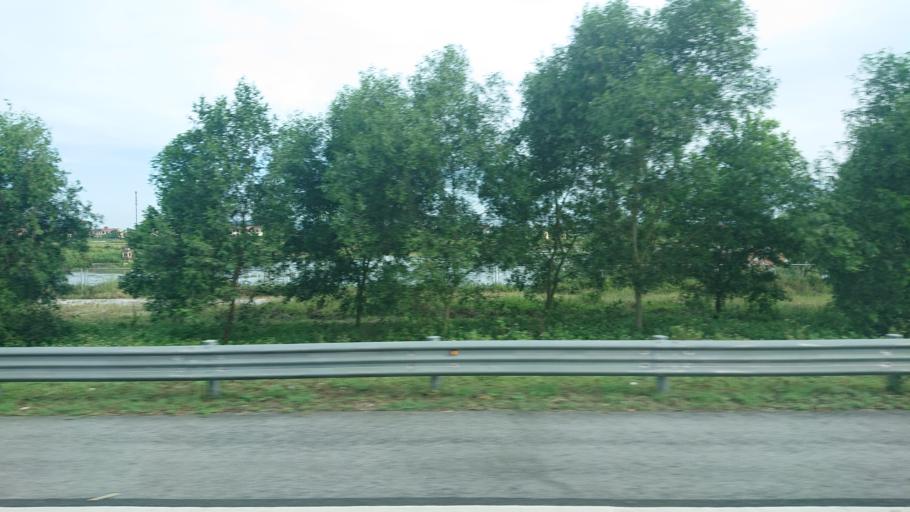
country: VN
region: Hai Phong
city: Nui Doi
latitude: 20.7656
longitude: 106.6533
